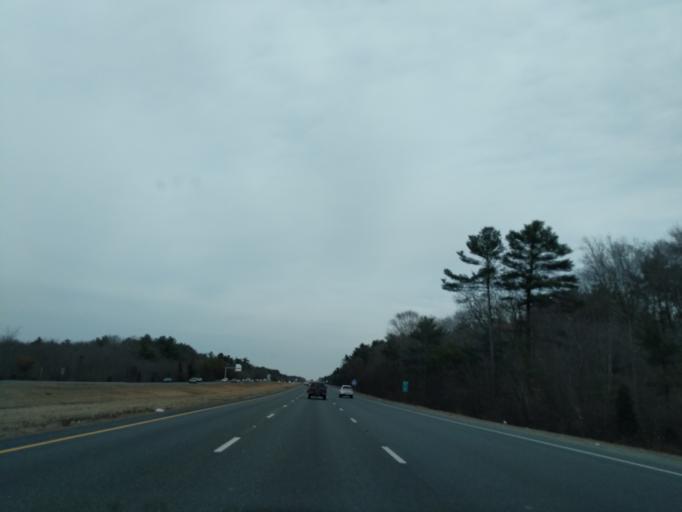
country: US
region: Massachusetts
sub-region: Bristol County
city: Raynham
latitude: 41.9616
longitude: -71.1153
